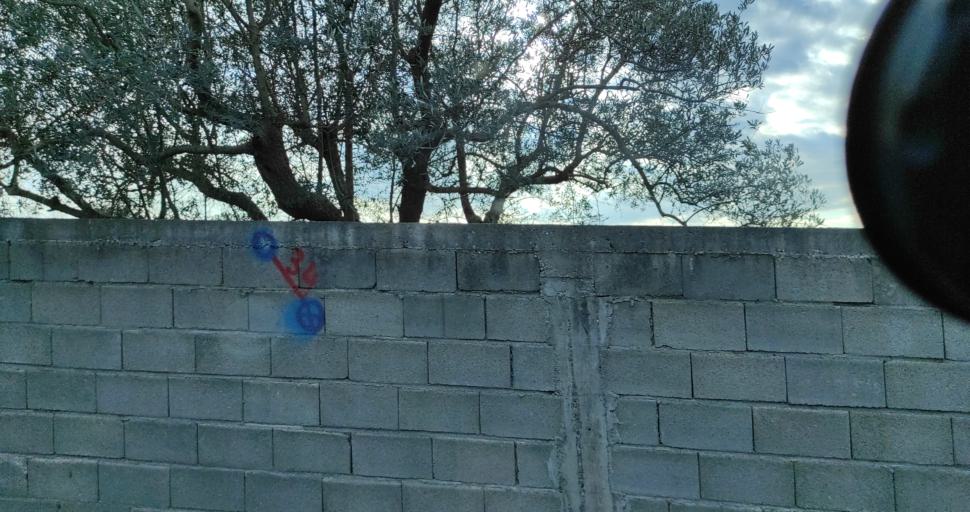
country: AL
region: Lezhe
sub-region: Rrethi i Lezhes
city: Kallmeti i Madh
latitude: 41.8796
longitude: 19.6650
